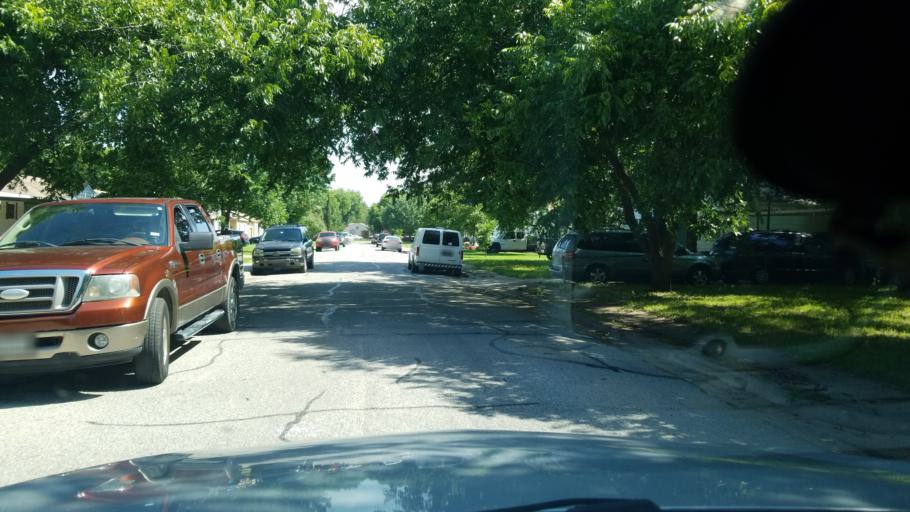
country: US
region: Texas
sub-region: Dallas County
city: Irving
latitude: 32.8145
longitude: -96.9674
